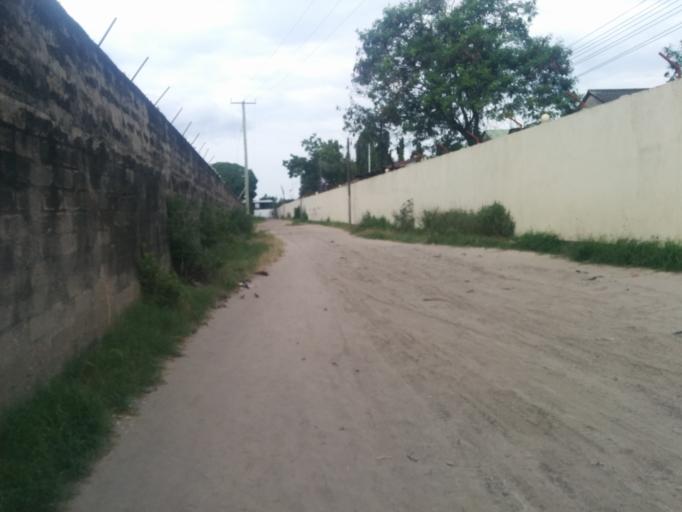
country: TZ
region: Dar es Salaam
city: Dar es Salaam
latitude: -6.8315
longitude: 39.2714
